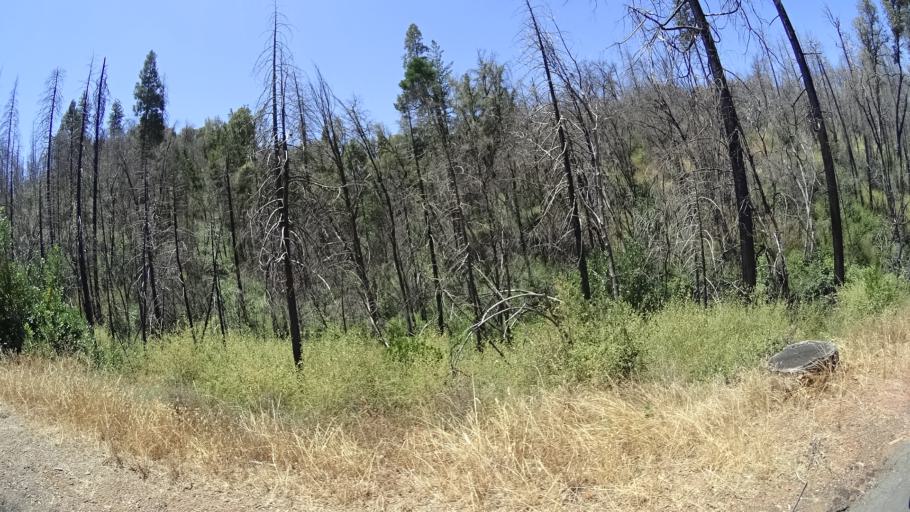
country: US
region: California
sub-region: Calaveras County
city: Mountain Ranch
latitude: 38.2457
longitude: -120.5771
